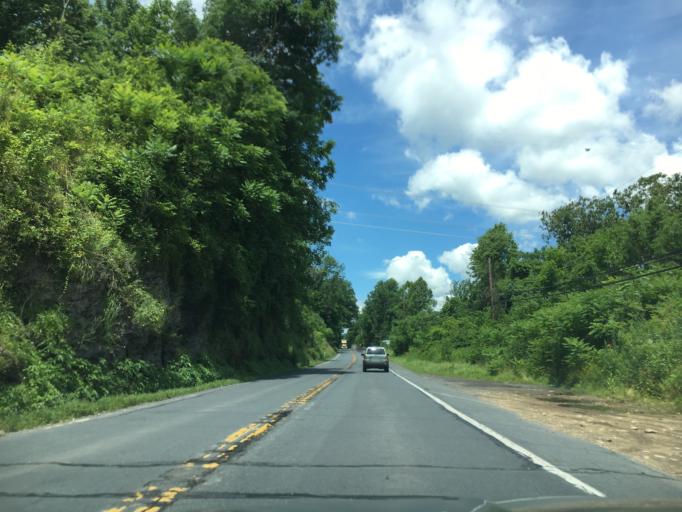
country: US
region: Pennsylvania
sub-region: Lehigh County
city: Laurys Station
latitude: 40.7134
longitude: -75.5238
